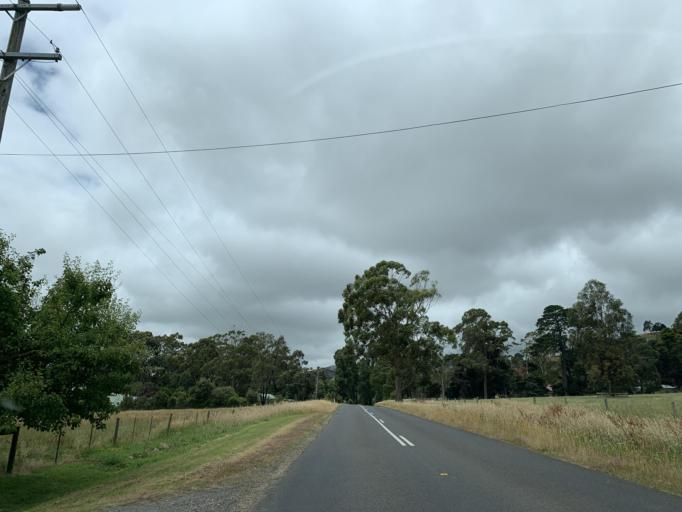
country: AU
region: Victoria
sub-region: Baw Baw
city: Warragul
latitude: -38.2448
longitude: 145.9842
